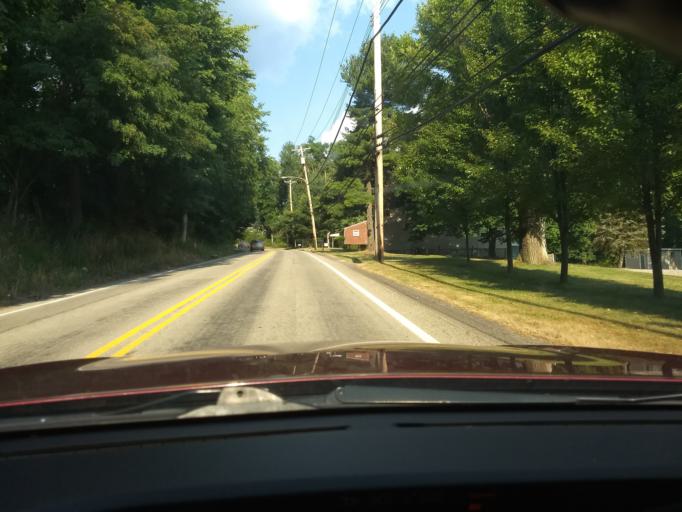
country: US
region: Pennsylvania
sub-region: Allegheny County
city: Plum
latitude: 40.4776
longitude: -79.7383
